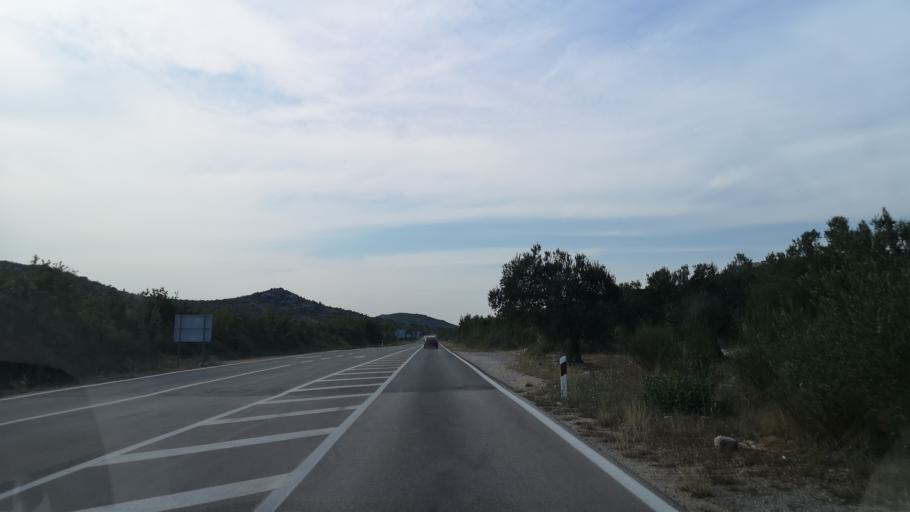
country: HR
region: Sibensko-Kniniska
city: Zaton
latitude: 43.8255
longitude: 15.7825
